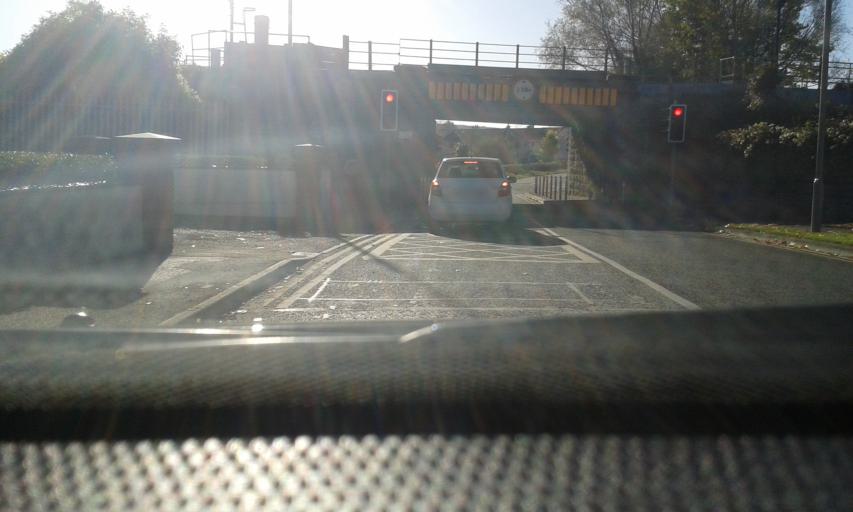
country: IE
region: Leinster
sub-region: Kildare
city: Monasterevin
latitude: 53.1472
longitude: -7.0555
